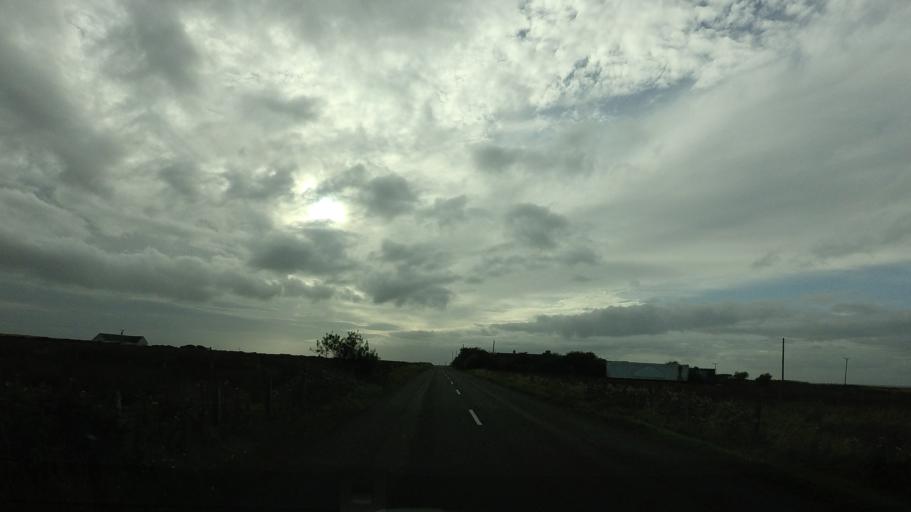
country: GB
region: Scotland
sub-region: Highland
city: Wick
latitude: 58.6422
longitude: -3.0908
